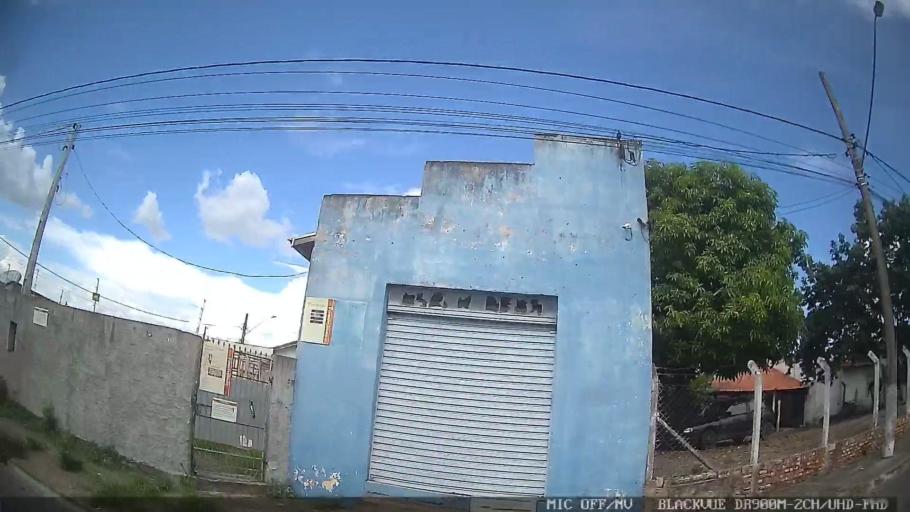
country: BR
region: Sao Paulo
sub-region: Conchas
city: Conchas
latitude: -23.0146
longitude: -48.0137
